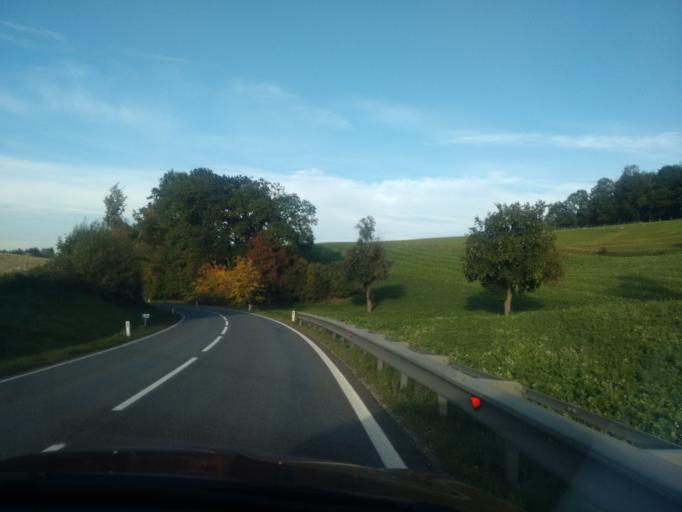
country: AT
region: Upper Austria
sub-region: Politischer Bezirk Vocklabruck
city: Niederthalheim
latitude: 48.1533
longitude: 13.7337
